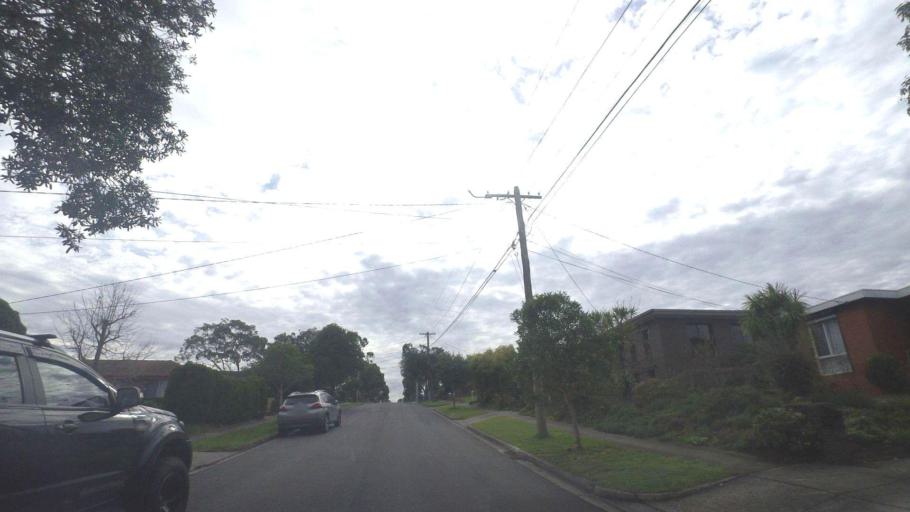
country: AU
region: Victoria
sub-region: Manningham
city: Templestowe Lower
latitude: -37.7628
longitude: 145.1029
